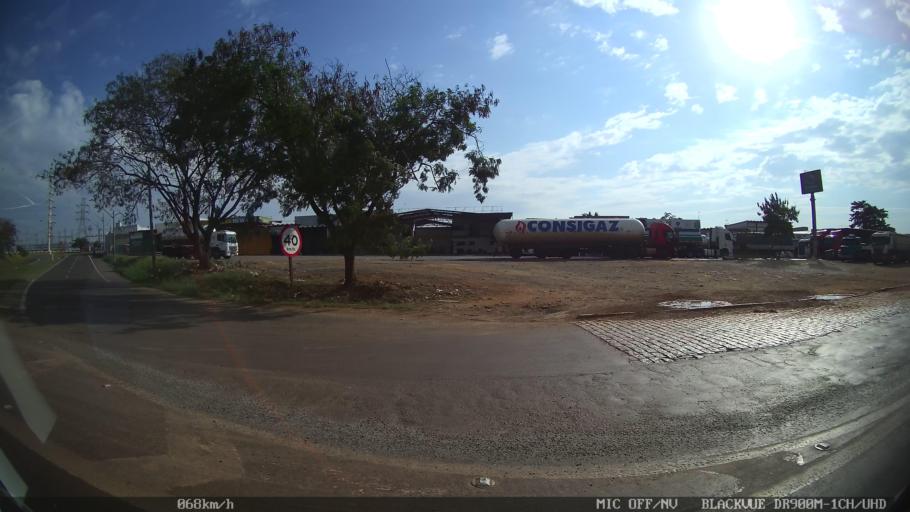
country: BR
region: Sao Paulo
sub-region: Paulinia
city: Paulinia
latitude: -22.7925
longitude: -47.1357
